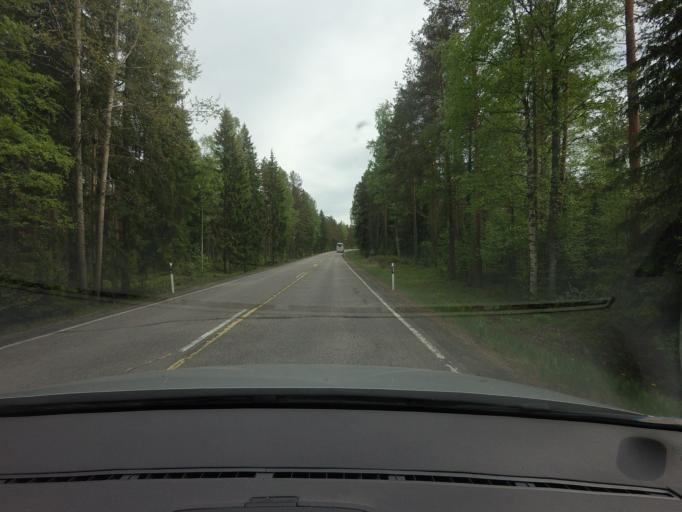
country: FI
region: Kymenlaakso
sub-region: Kotka-Hamina
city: Hamina
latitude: 60.7632
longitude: 27.3485
